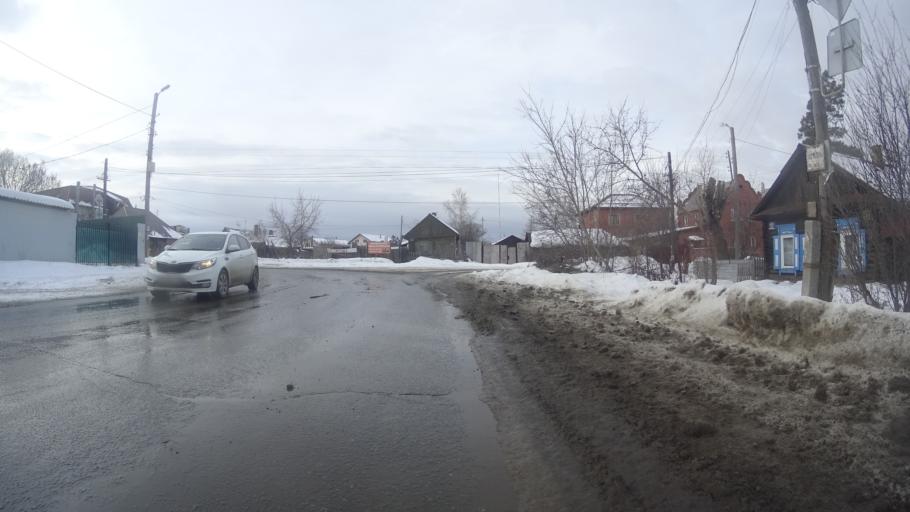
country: RU
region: Chelyabinsk
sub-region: Gorod Chelyabinsk
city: Chelyabinsk
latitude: 55.1306
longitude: 61.3958
